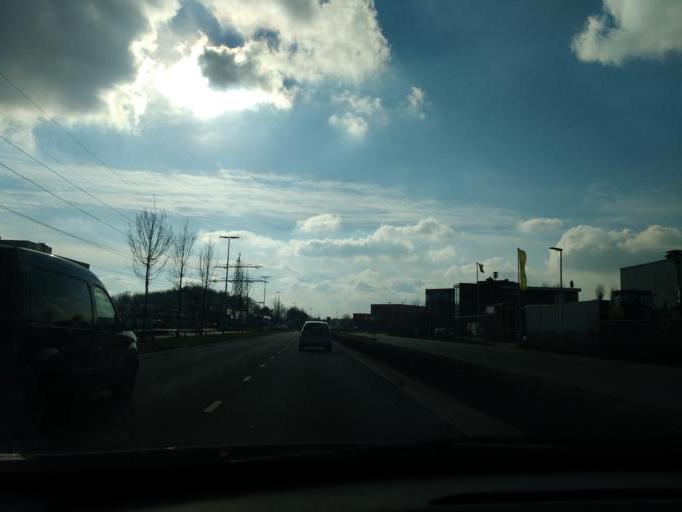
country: NL
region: Gelderland
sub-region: Gemeente Nijmegen
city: Nijmegen
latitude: 51.8453
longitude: 5.8264
